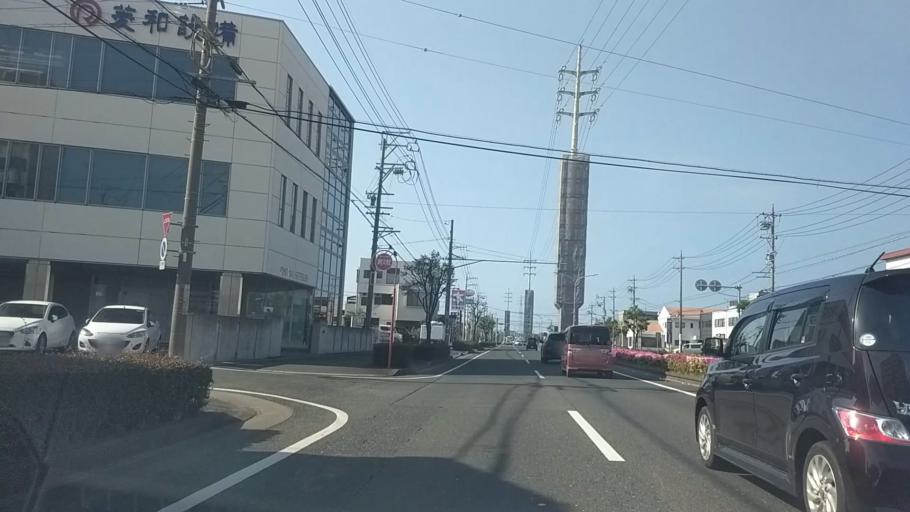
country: JP
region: Shizuoka
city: Hamamatsu
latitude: 34.7072
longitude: 137.7582
